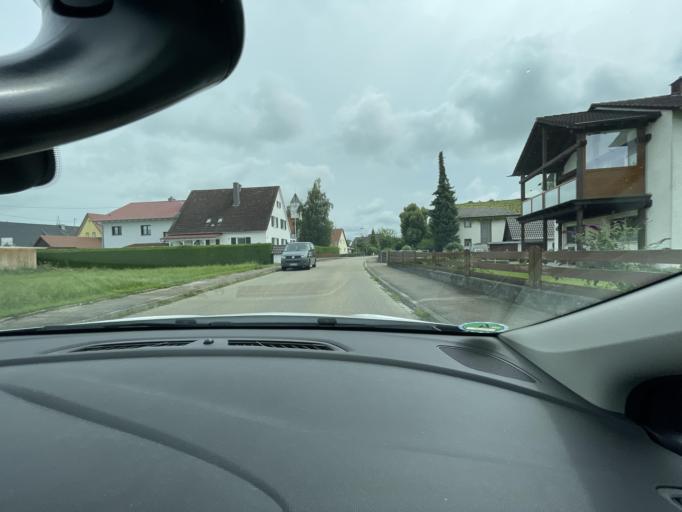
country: DE
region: Bavaria
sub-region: Swabia
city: Meitingen
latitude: 48.5652
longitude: 10.8607
